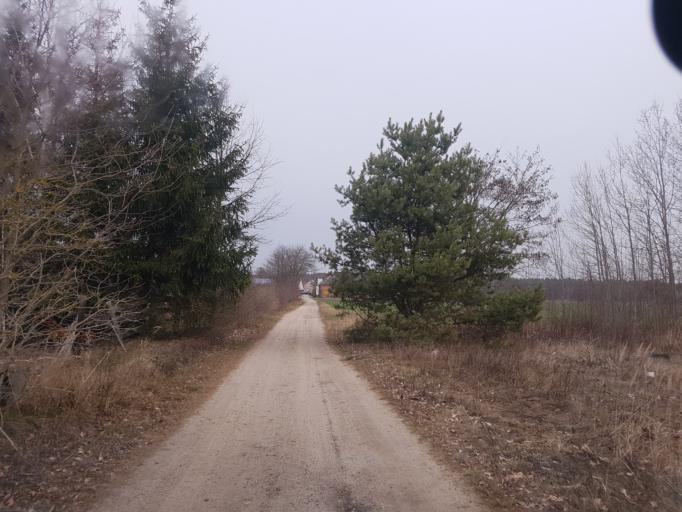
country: DE
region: Brandenburg
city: Finsterwalde
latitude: 51.6612
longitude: 13.6868
